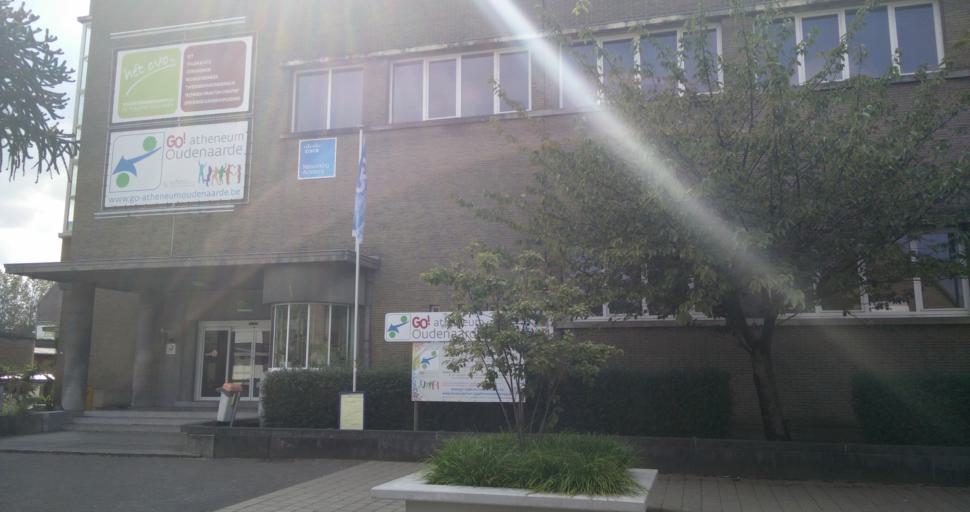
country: BE
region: Flanders
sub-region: Provincie Oost-Vlaanderen
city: Oudenaarde
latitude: 50.8482
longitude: 3.6138
